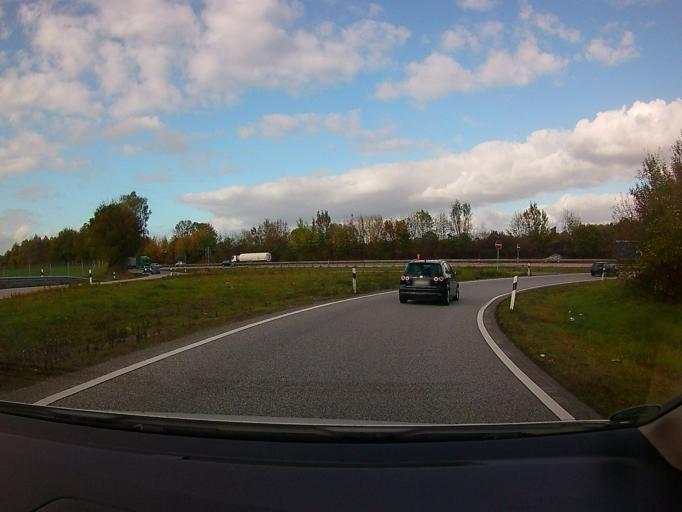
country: DE
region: Schleswig-Holstein
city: Kasseburg
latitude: 53.5598
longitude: 10.4073
